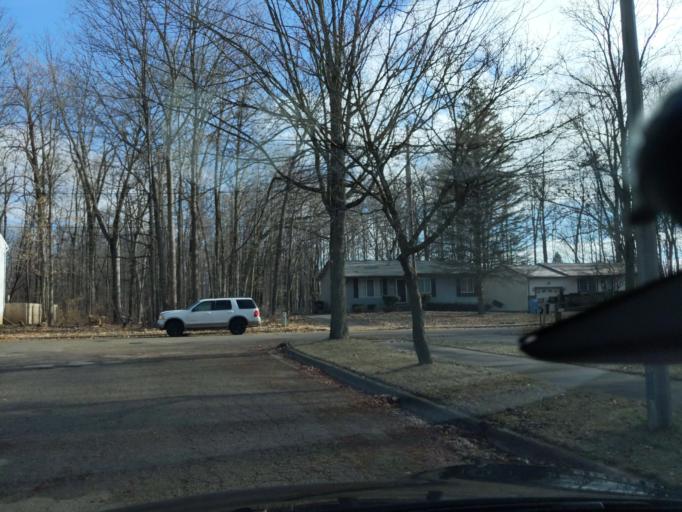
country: US
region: Michigan
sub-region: Ingham County
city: Lansing
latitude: 42.6805
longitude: -84.5875
